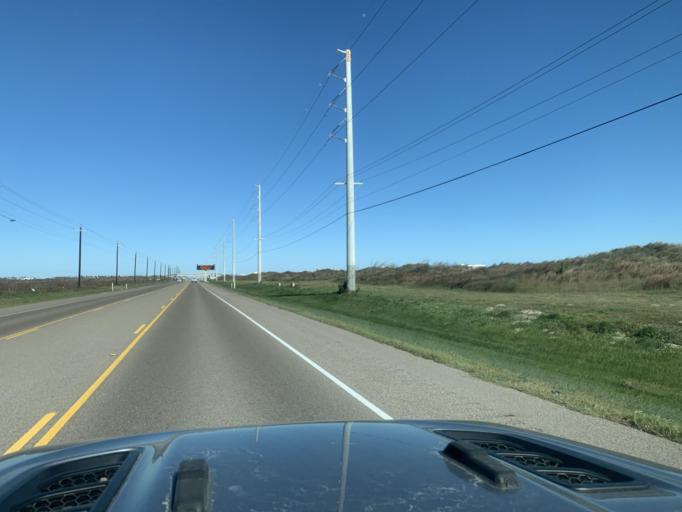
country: US
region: Texas
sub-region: Nueces County
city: Port Aransas
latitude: 27.7911
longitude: -97.0953
